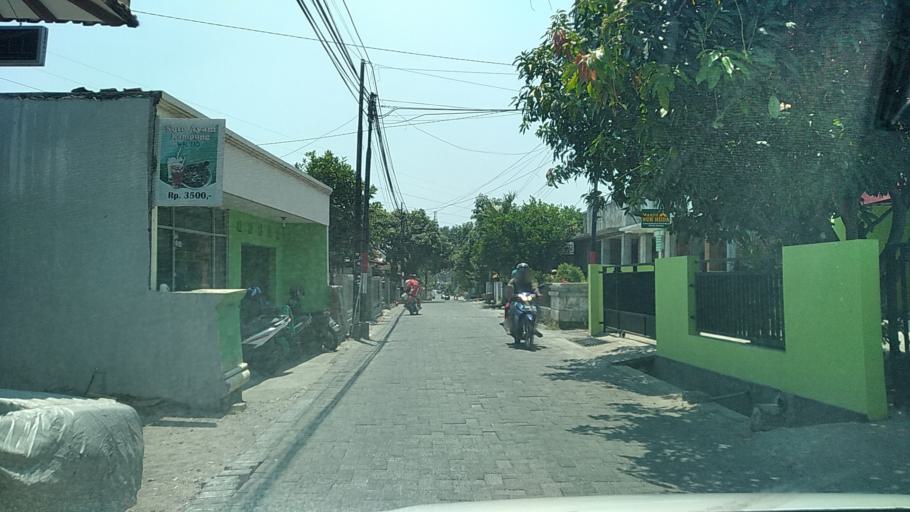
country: ID
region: Central Java
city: Semarang
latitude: -7.0197
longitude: 110.3862
